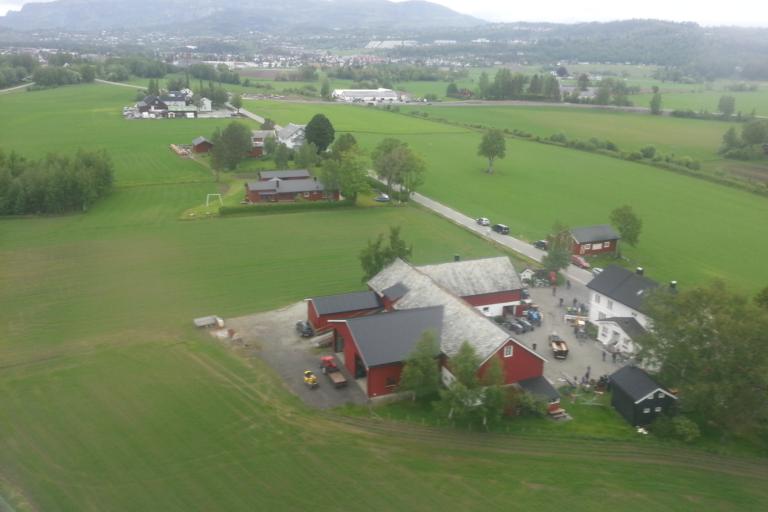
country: NO
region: Nord-Trondelag
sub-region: Stjordal
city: Stjordalshalsen
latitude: 63.4576
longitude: 10.9477
